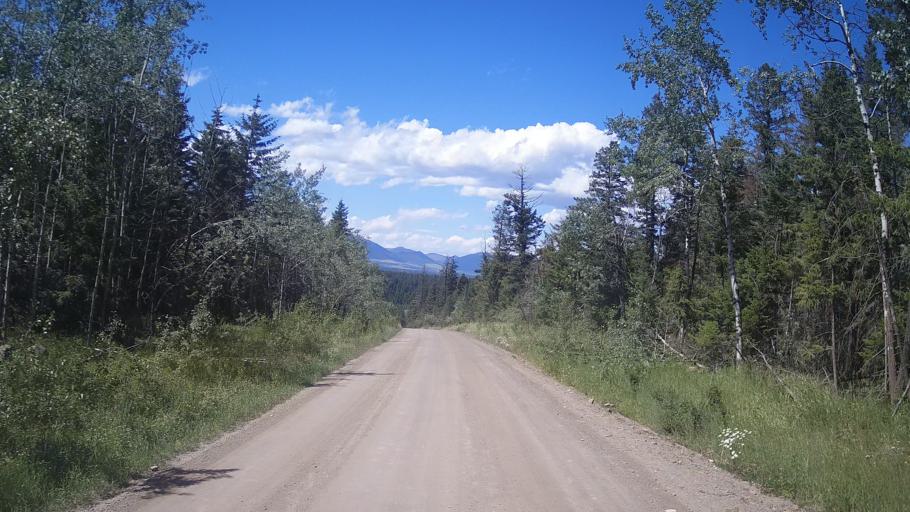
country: CA
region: British Columbia
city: Cache Creek
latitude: 51.1536
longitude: -121.5411
